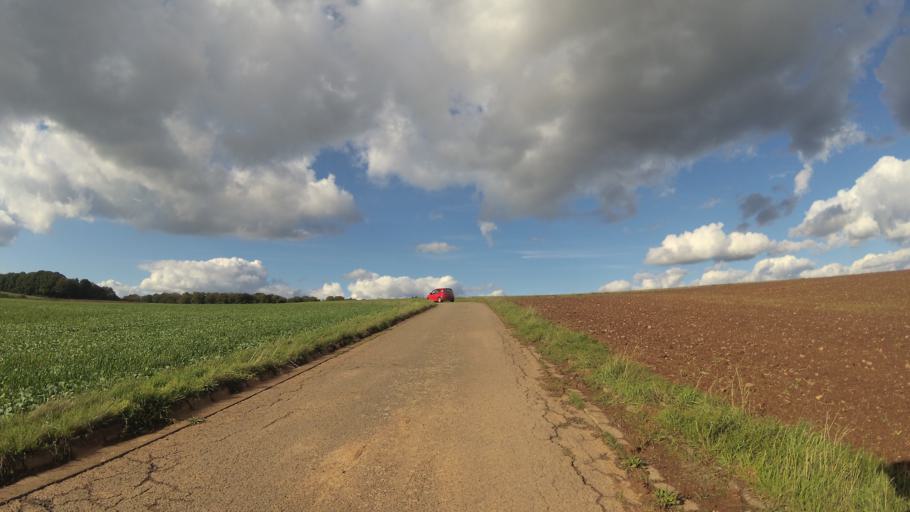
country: DE
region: Saarland
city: Marpingen
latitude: 49.4422
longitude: 7.0760
